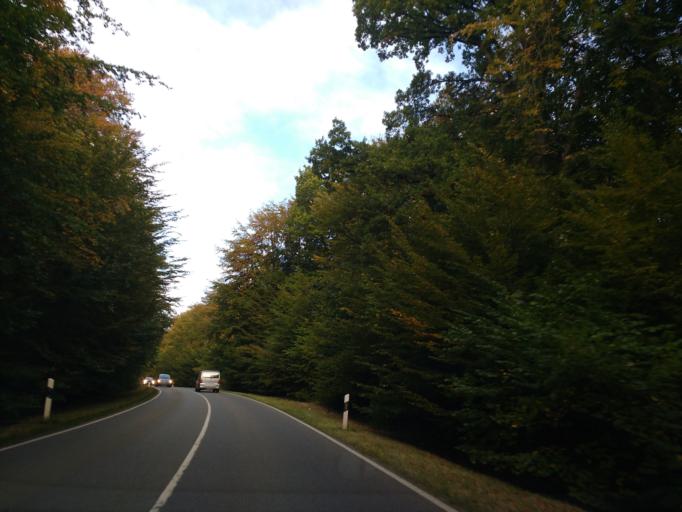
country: DE
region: Schleswig-Holstein
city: Schonwalde am Bungsberg
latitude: 54.1780
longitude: 10.7742
